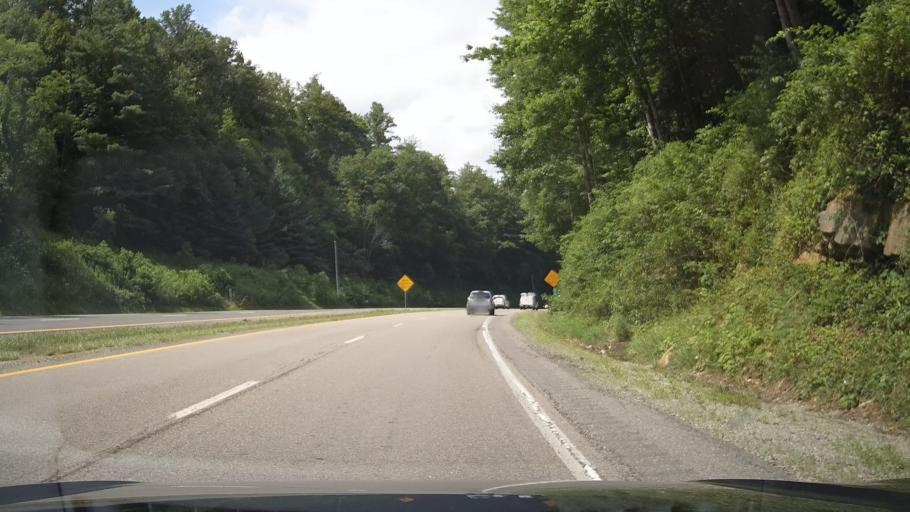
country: US
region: Virginia
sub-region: Wise County
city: Wise
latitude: 37.0146
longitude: -82.5912
